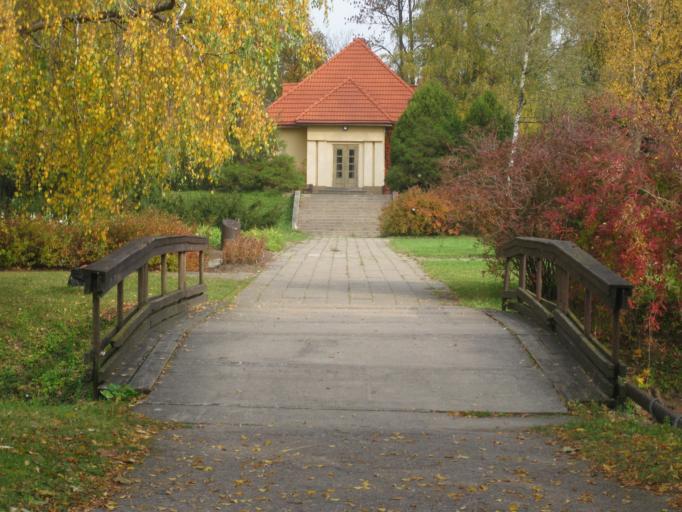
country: LT
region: Kauno apskritis
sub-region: Kaunas
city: Aleksotas
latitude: 54.8698
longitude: 23.9098
